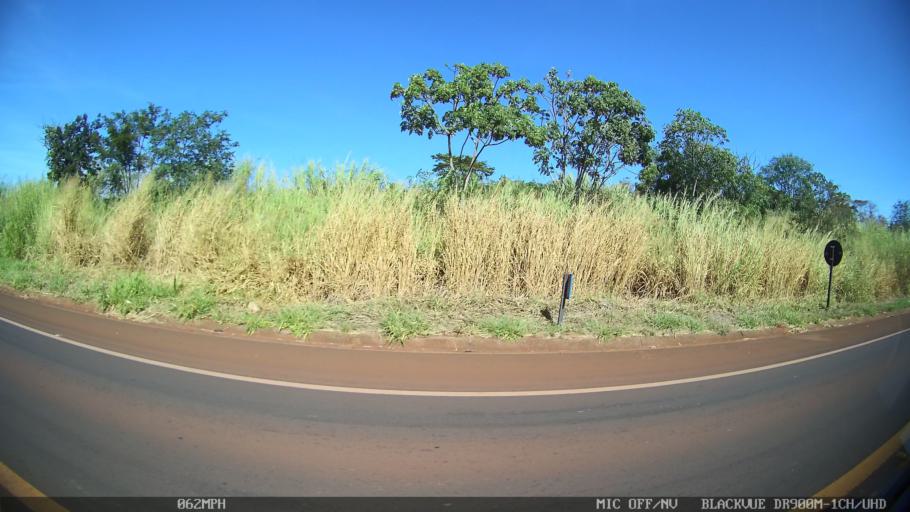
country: BR
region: Sao Paulo
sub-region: Ipua
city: Ipua
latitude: -20.4930
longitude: -48.0181
